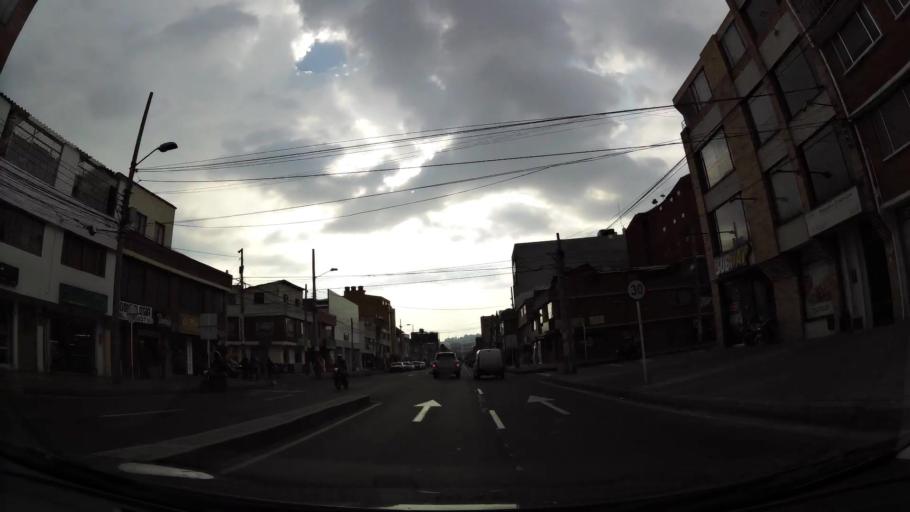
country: CO
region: Bogota D.C.
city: Barrio San Luis
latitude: 4.7161
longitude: -74.0573
